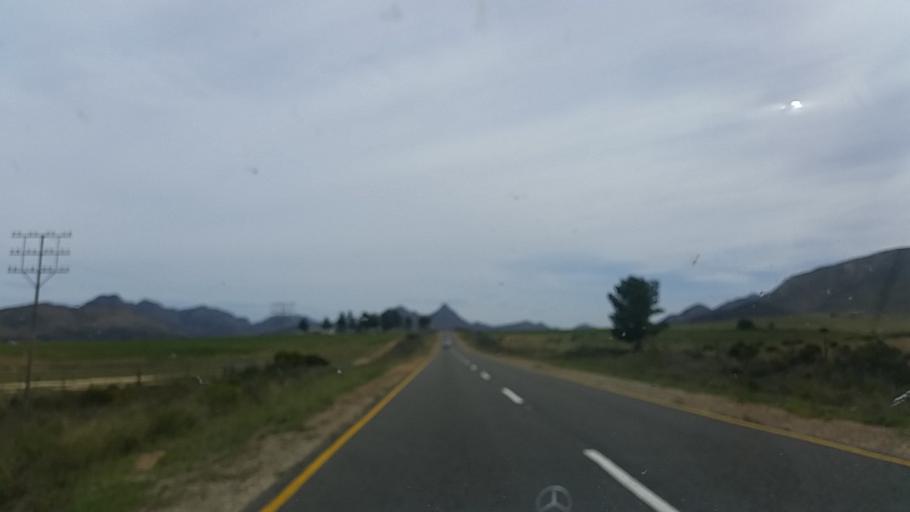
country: ZA
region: Western Cape
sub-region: Eden District Municipality
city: George
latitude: -33.8183
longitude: 22.5040
